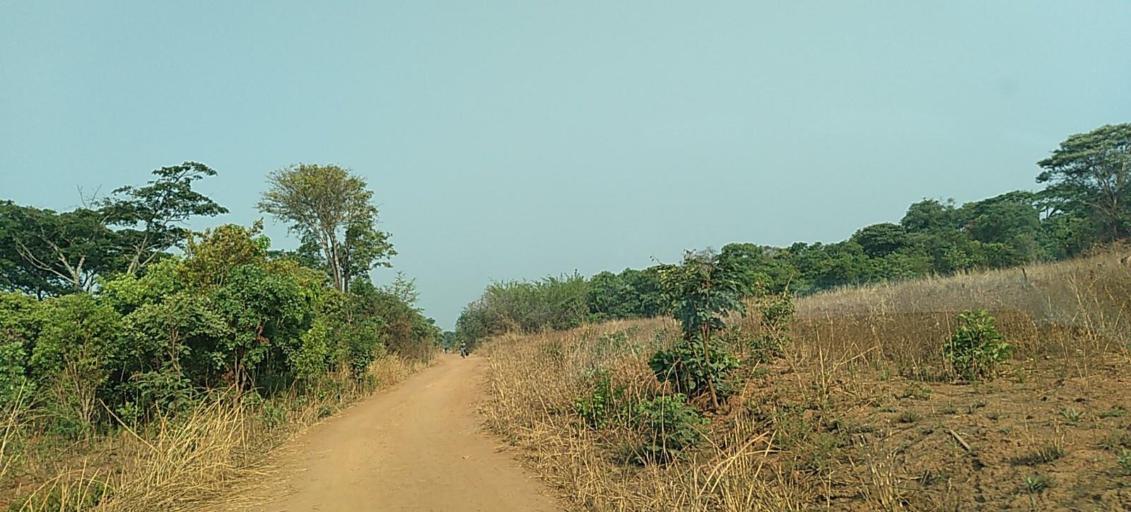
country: ZM
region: Copperbelt
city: Chingola
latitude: -12.8550
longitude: 27.5578
